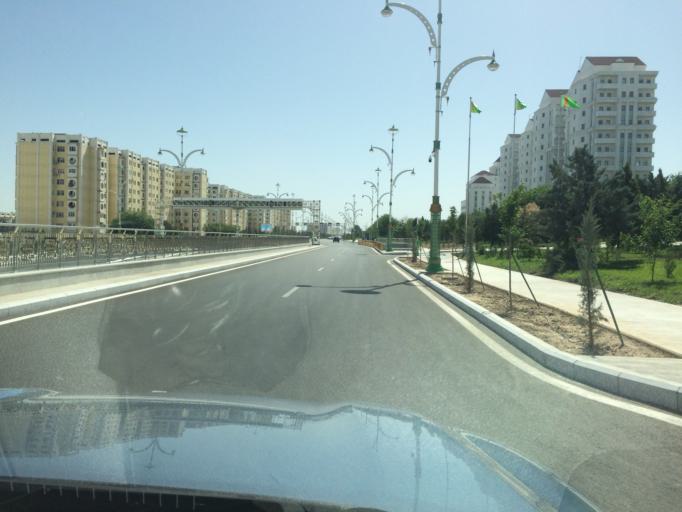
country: TM
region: Ahal
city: Ashgabat
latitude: 37.8953
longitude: 58.3898
